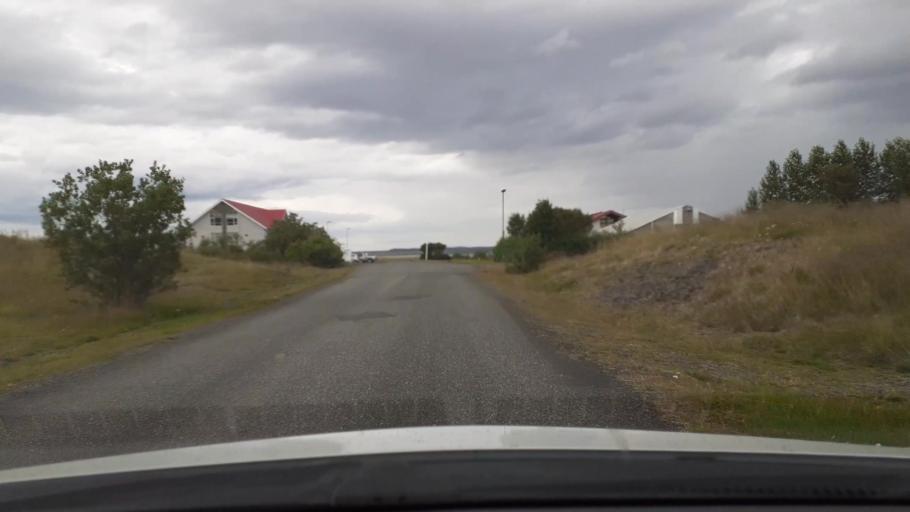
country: IS
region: West
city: Borgarnes
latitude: 64.5620
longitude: -21.7676
